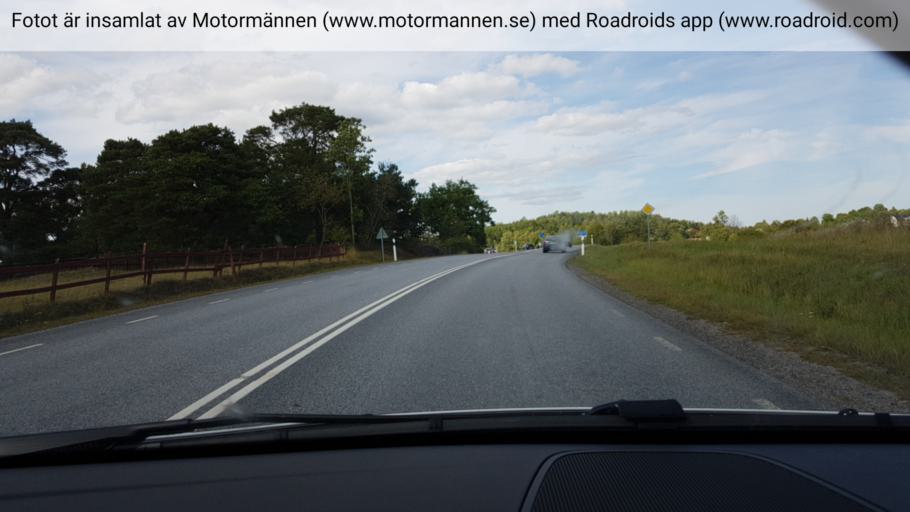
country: SE
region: Stockholm
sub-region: Sodertalje Kommun
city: Pershagen
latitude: 59.0828
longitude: 17.6077
